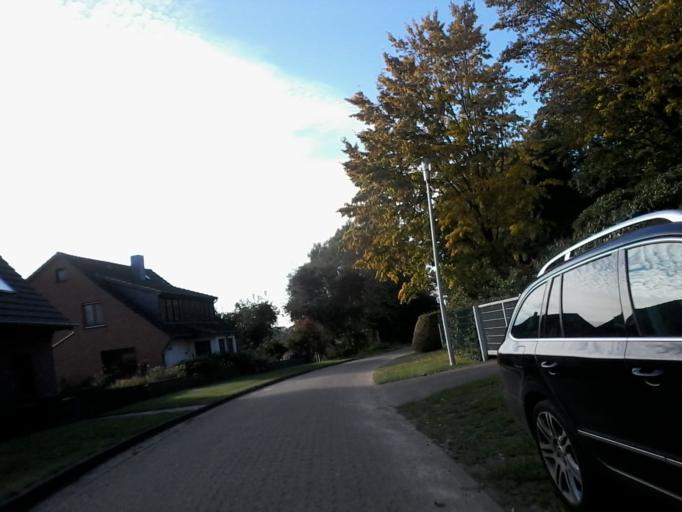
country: DE
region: Lower Saxony
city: Achim
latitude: 52.9999
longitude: 9.0441
